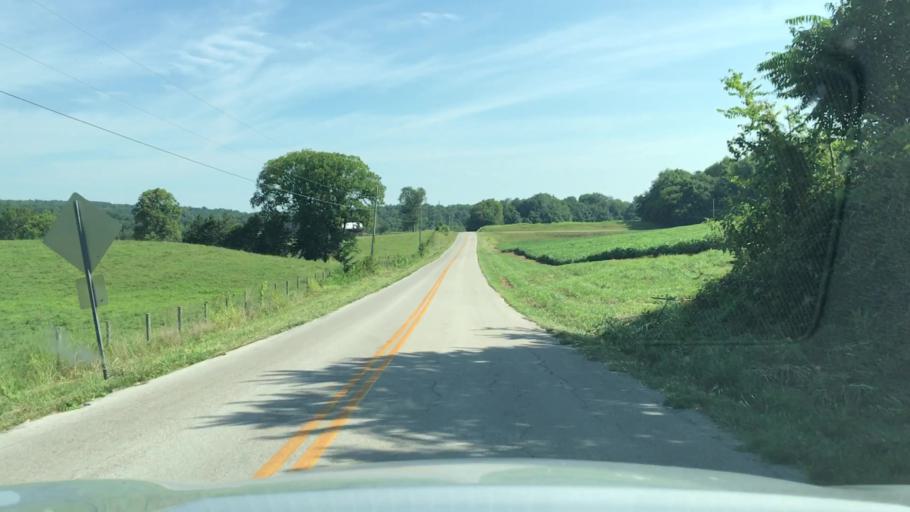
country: US
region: Kentucky
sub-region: Clinton County
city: Albany
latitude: 36.7354
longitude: -85.0142
